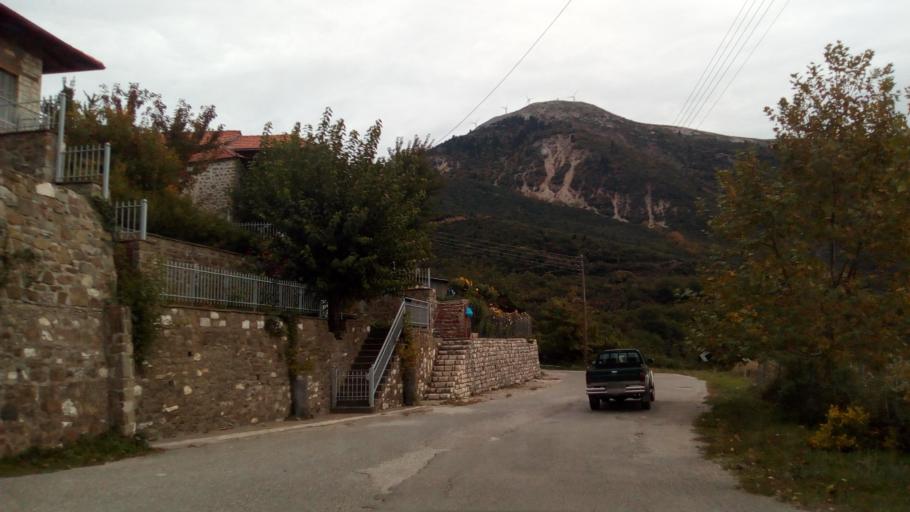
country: GR
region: West Greece
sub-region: Nomos Aitolias kai Akarnanias
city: Thermo
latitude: 38.6025
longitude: 21.7915
